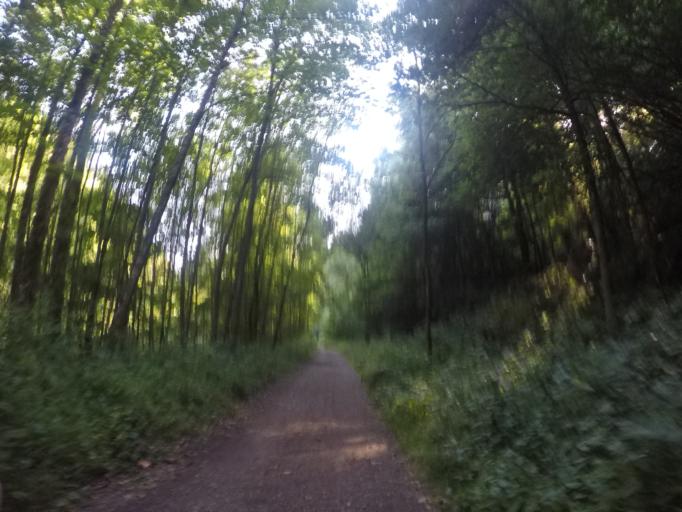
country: LU
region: Luxembourg
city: Itzig
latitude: 49.6016
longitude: 6.1633
